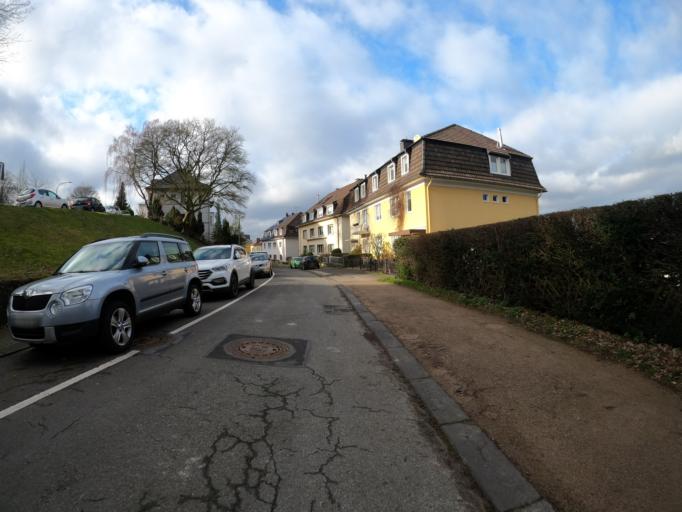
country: DE
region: North Rhine-Westphalia
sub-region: Regierungsbezirk Dusseldorf
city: Wuppertal
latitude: 51.2471
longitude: 7.1567
